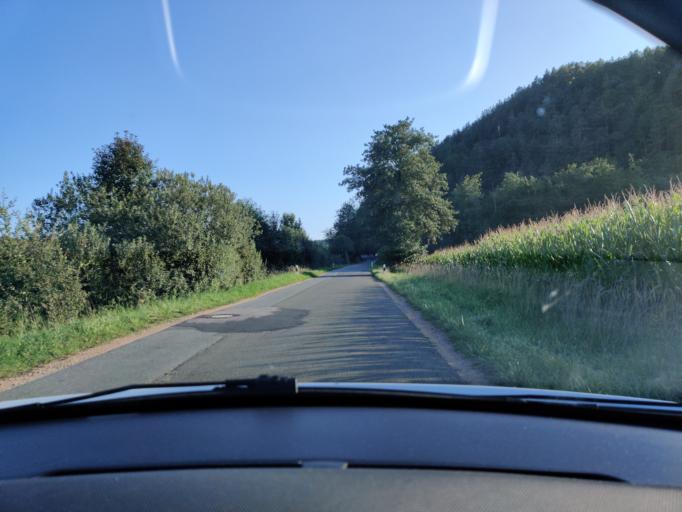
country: DE
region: Bavaria
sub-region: Upper Palatinate
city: Nabburg
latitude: 49.4332
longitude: 12.1694
